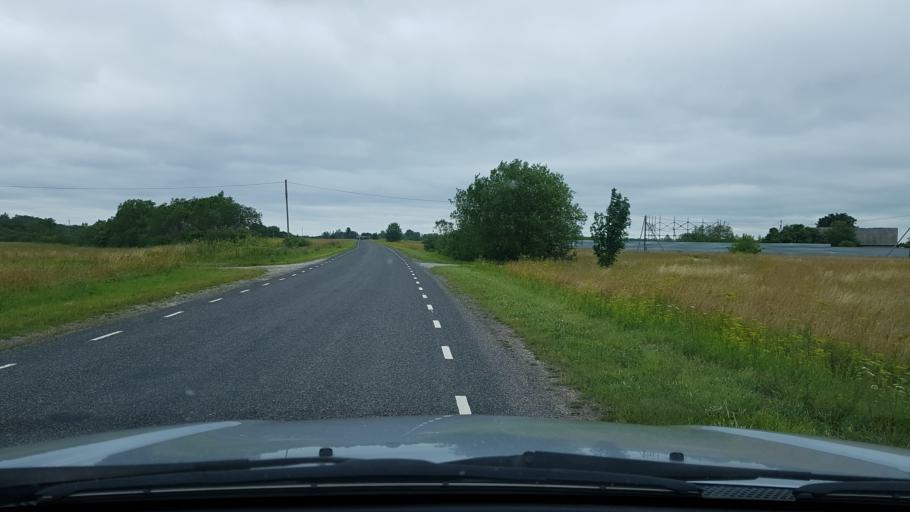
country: EE
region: Ida-Virumaa
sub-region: Narva linn
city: Narva
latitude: 59.3774
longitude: 28.1210
